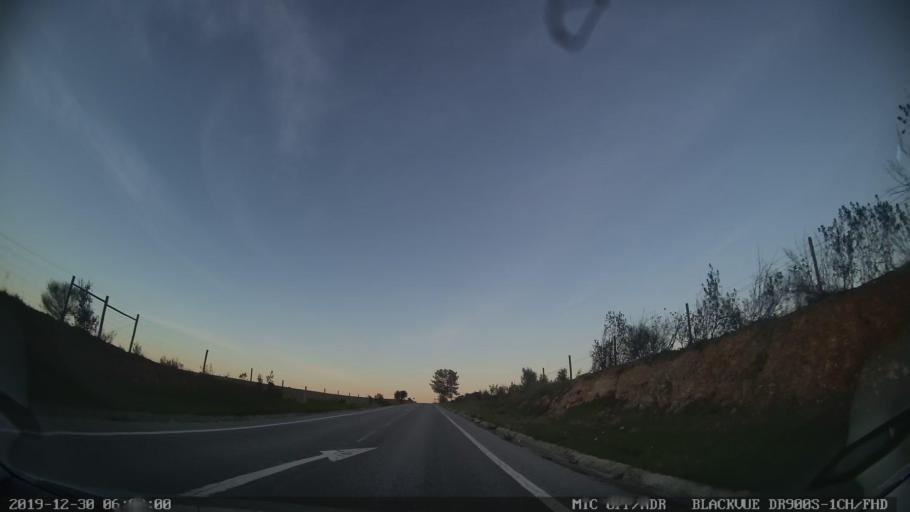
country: PT
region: Castelo Branco
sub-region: Penamacor
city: Penamacor
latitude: 40.0659
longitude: -7.2433
